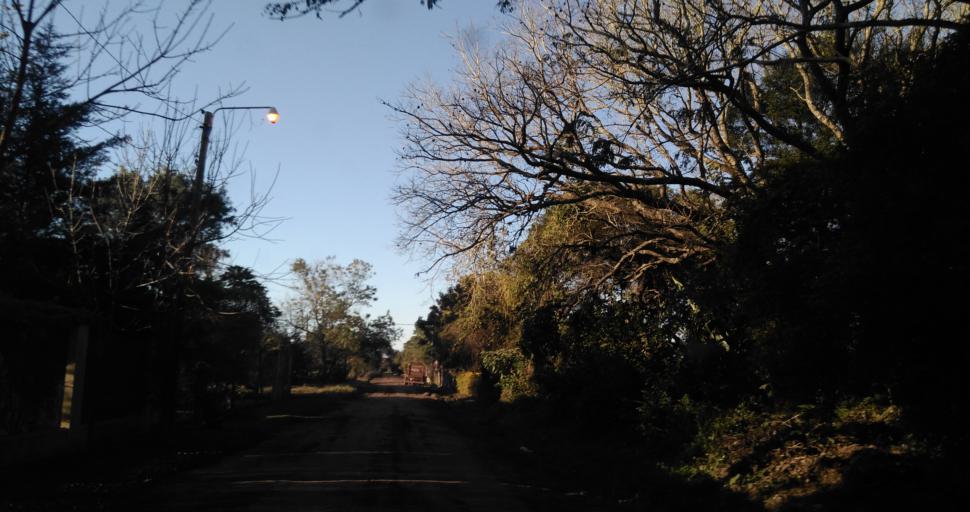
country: AR
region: Chaco
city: Colonia Benitez
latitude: -27.3293
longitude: -58.9563
